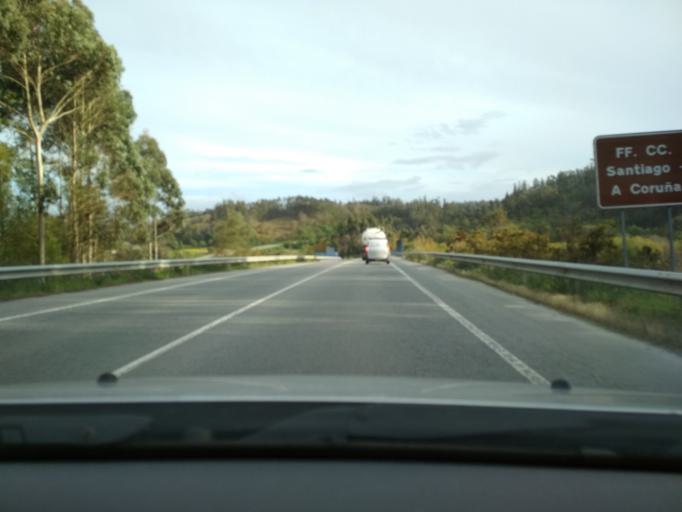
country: ES
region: Galicia
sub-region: Provincia da Coruna
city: Cerceda
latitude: 43.2218
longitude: -8.4584
